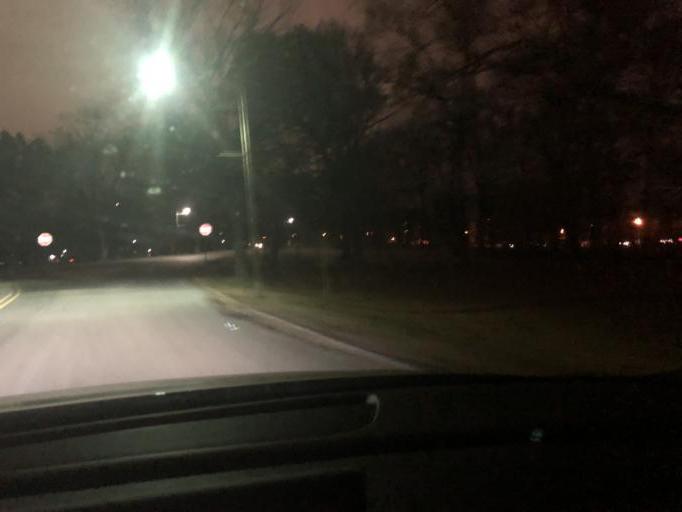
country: US
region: New Jersey
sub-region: Essex County
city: East Orange
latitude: 40.7579
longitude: -74.1845
